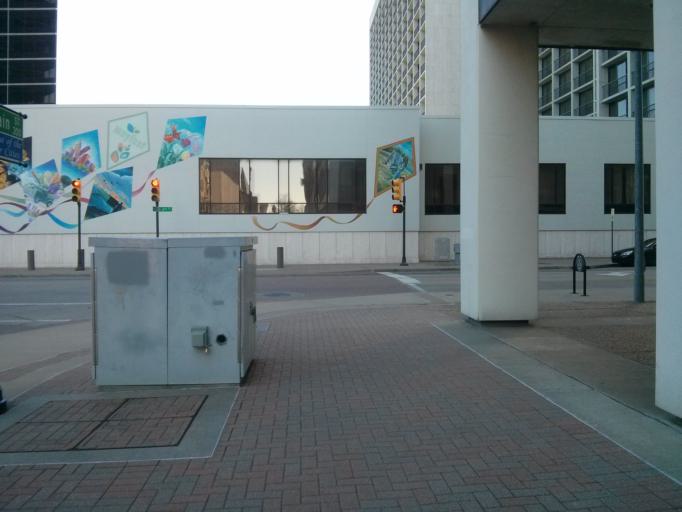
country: US
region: Oklahoma
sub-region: Tulsa County
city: Tulsa
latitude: 36.1536
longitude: -95.9922
